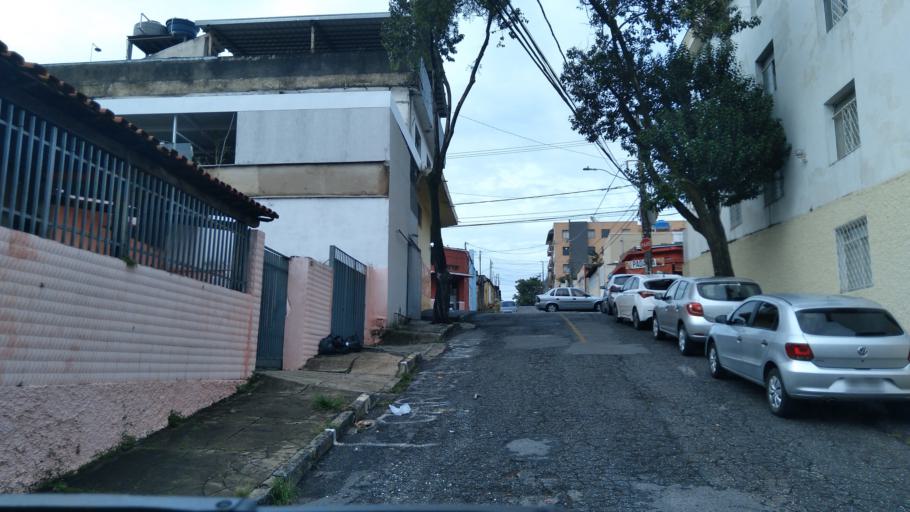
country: BR
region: Minas Gerais
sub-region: Contagem
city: Contagem
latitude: -19.9275
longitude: -43.9979
